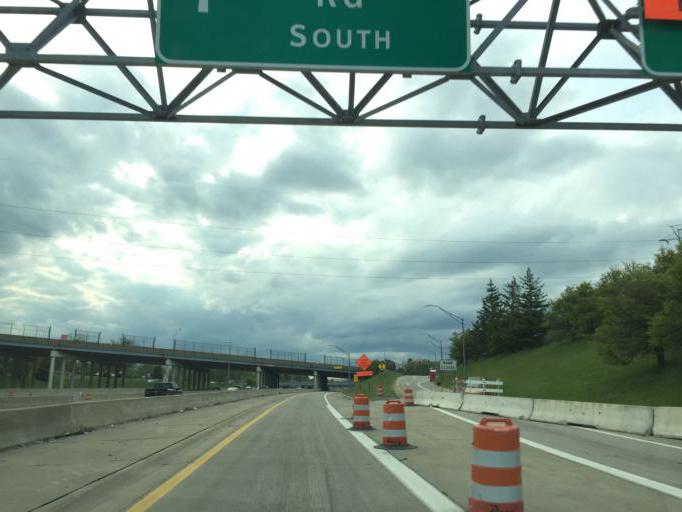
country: US
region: Michigan
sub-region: Wayne County
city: Dearborn Heights
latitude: 42.3795
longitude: -83.2347
